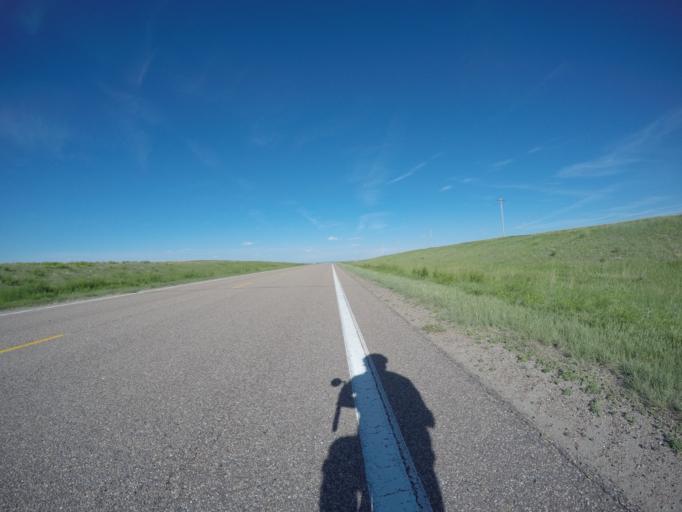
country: US
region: Kansas
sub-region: Cheyenne County
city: Saint Francis
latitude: 39.7567
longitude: -101.9462
